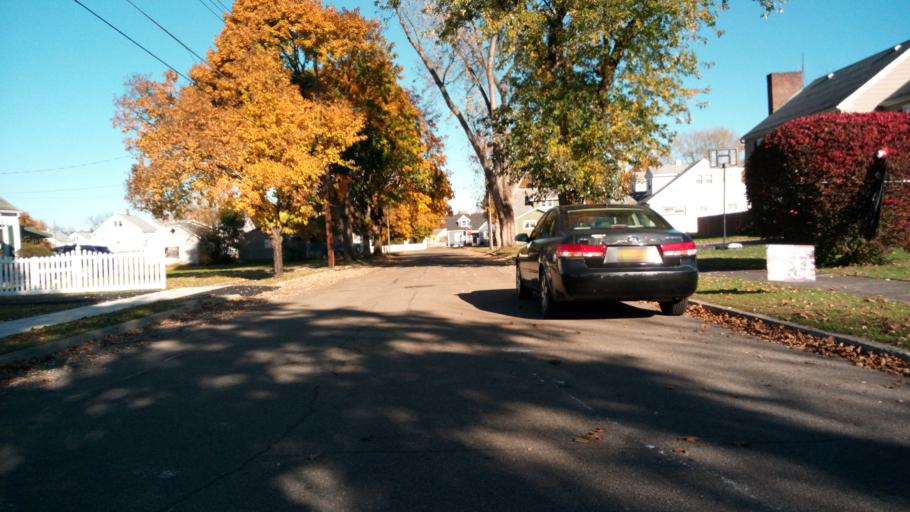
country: US
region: New York
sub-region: Chemung County
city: Southport
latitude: 42.0675
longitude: -76.8096
